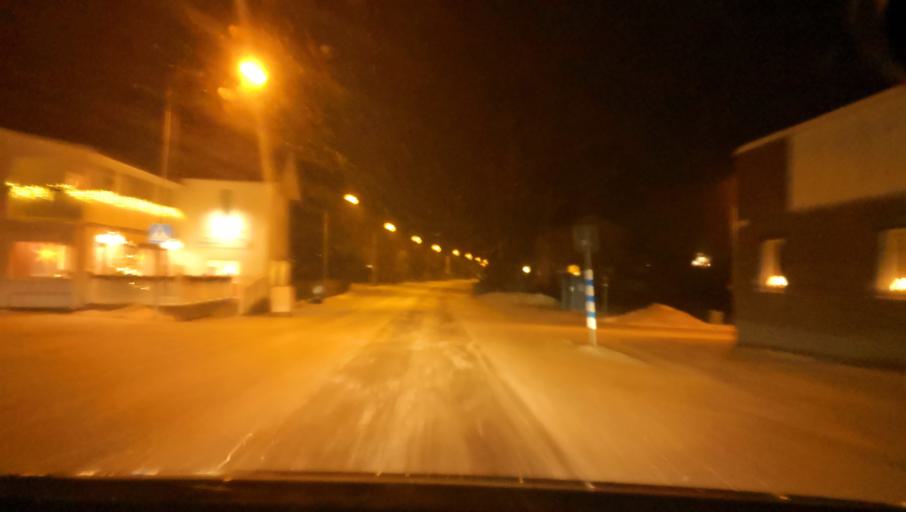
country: SE
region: Uppsala
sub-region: Heby Kommun
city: Tarnsjo
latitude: 60.1533
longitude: 16.9272
